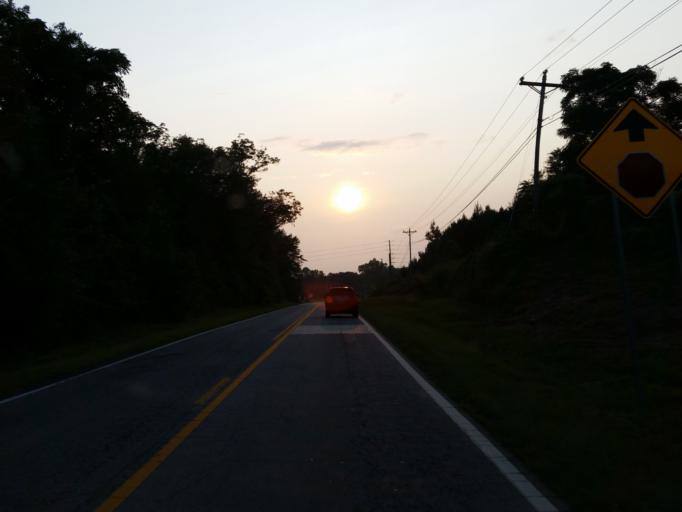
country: US
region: Georgia
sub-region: Spalding County
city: East Griffin
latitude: 33.2920
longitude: -84.1875
